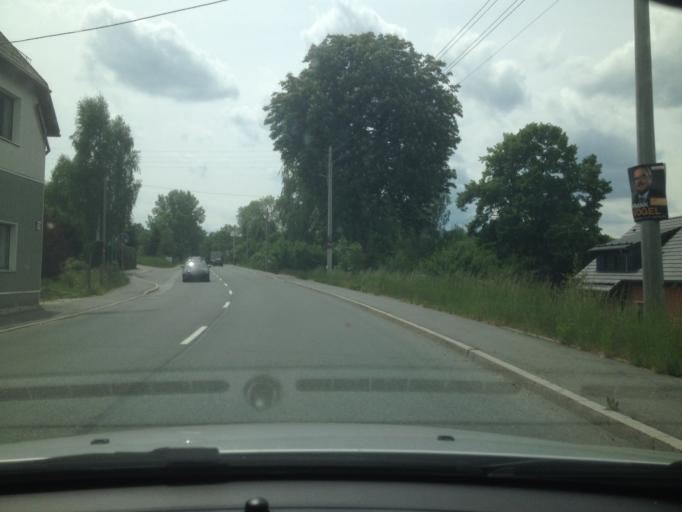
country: DE
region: Saxony
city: Stollberg
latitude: 50.6902
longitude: 12.7659
